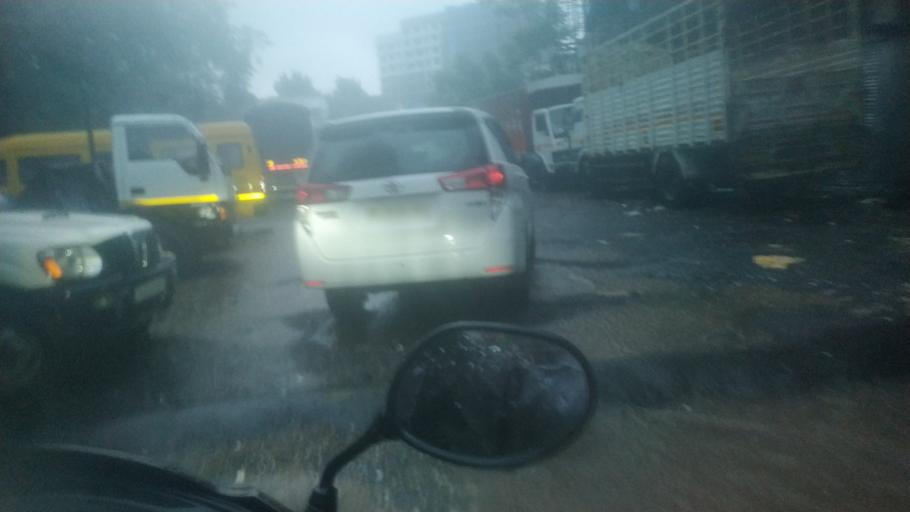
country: IN
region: Maharashtra
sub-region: Mumbai Suburban
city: Mumbai
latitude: 19.1143
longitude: 72.8535
